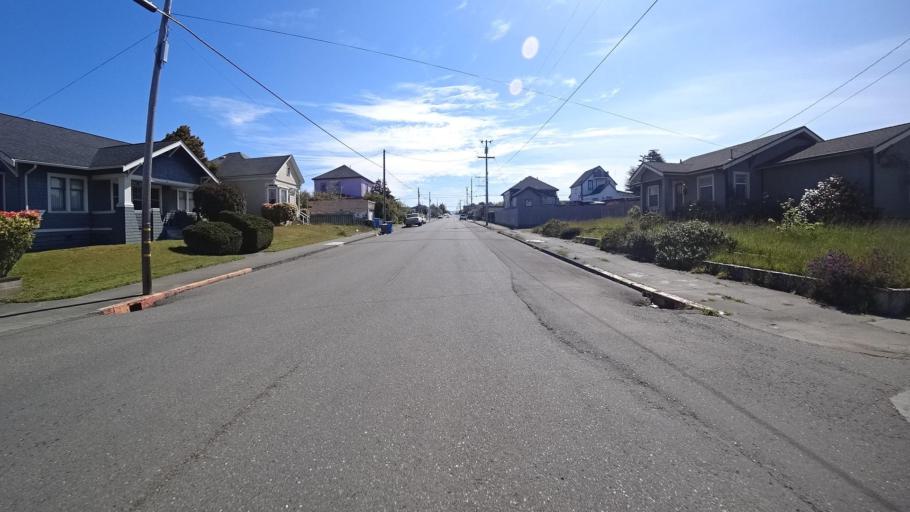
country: US
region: California
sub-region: Humboldt County
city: Bayview
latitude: 40.7862
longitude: -124.1783
